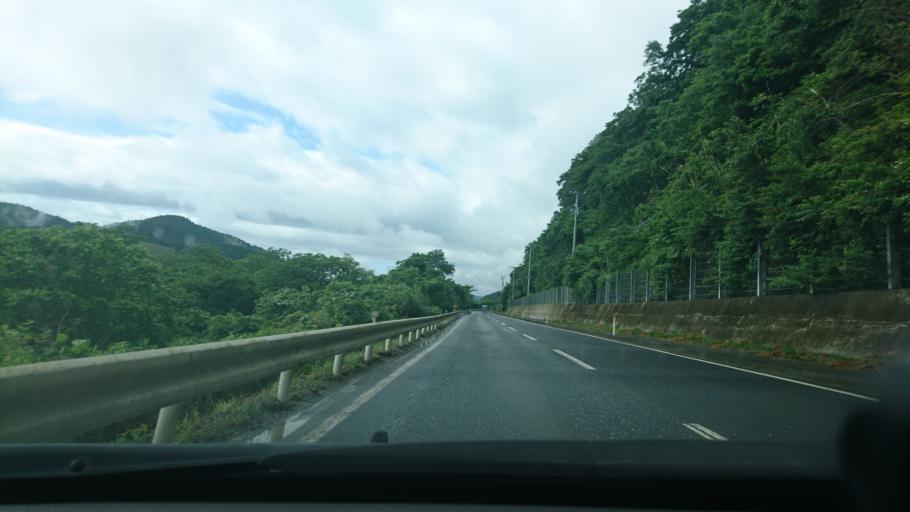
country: JP
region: Miyagi
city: Ishinomaki
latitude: 38.5847
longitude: 141.3042
